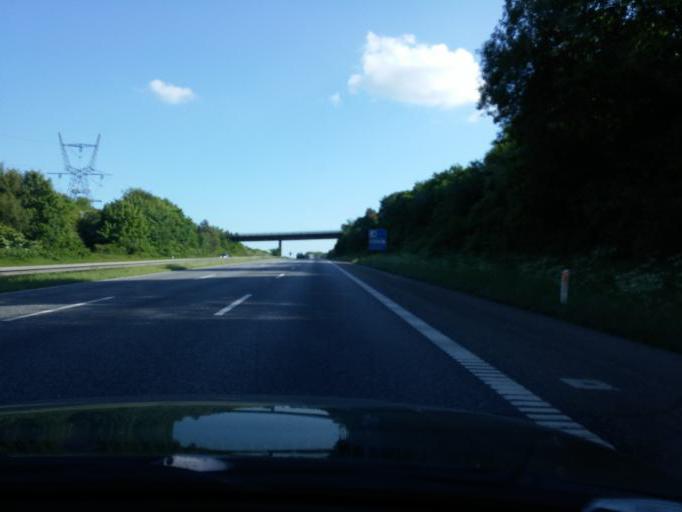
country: DK
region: South Denmark
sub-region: Kolding Kommune
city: Kolding
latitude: 55.4892
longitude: 9.4210
